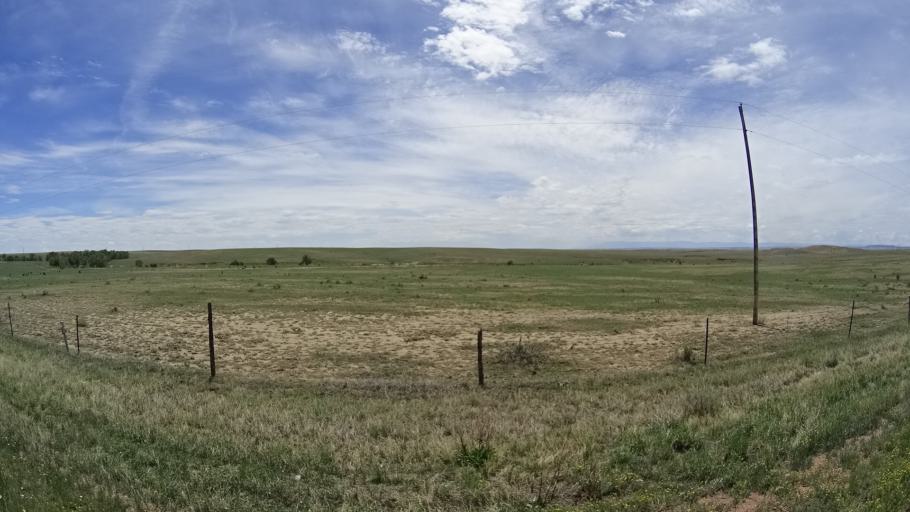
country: US
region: Colorado
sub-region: El Paso County
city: Fountain
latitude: 38.6940
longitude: -104.6060
